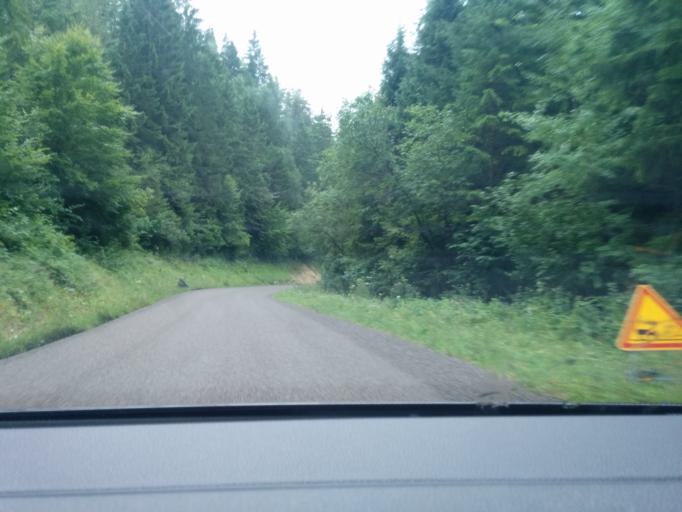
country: FR
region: Franche-Comte
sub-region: Departement du Jura
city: Saint-Lupicin
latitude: 46.4323
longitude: 5.8127
